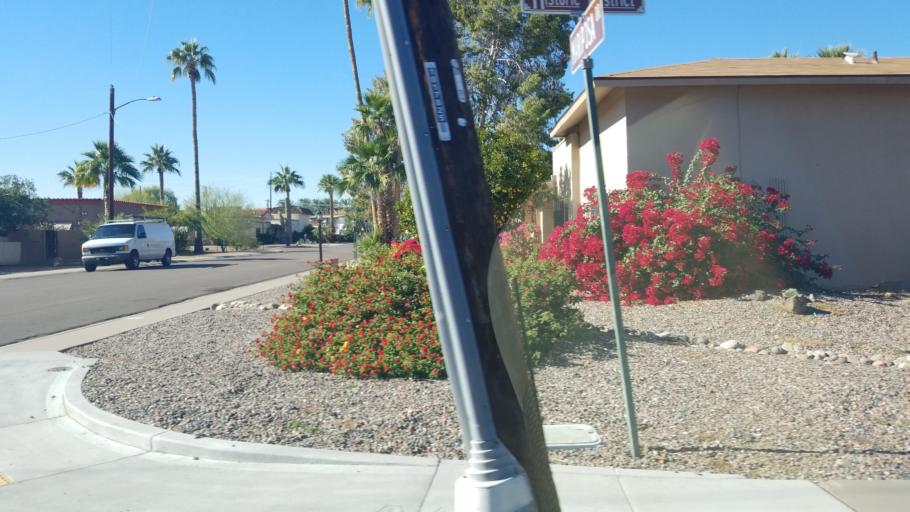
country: US
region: Arizona
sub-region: Maricopa County
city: Scottsdale
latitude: 33.5081
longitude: -111.9175
